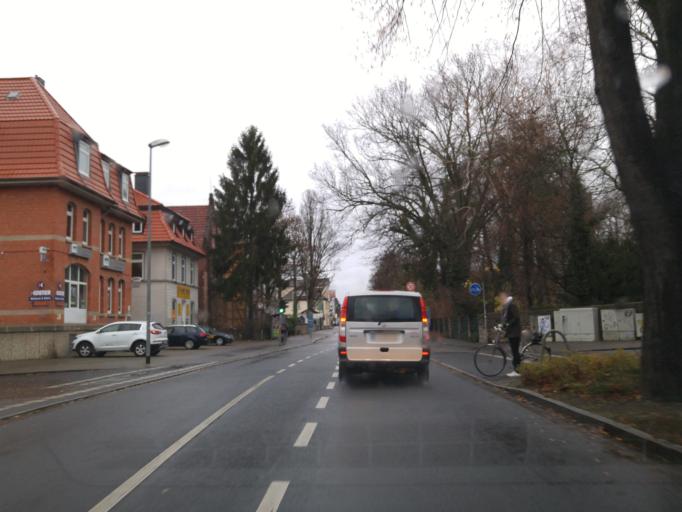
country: DE
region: Lower Saxony
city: Goettingen
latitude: 51.5252
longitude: 9.9397
